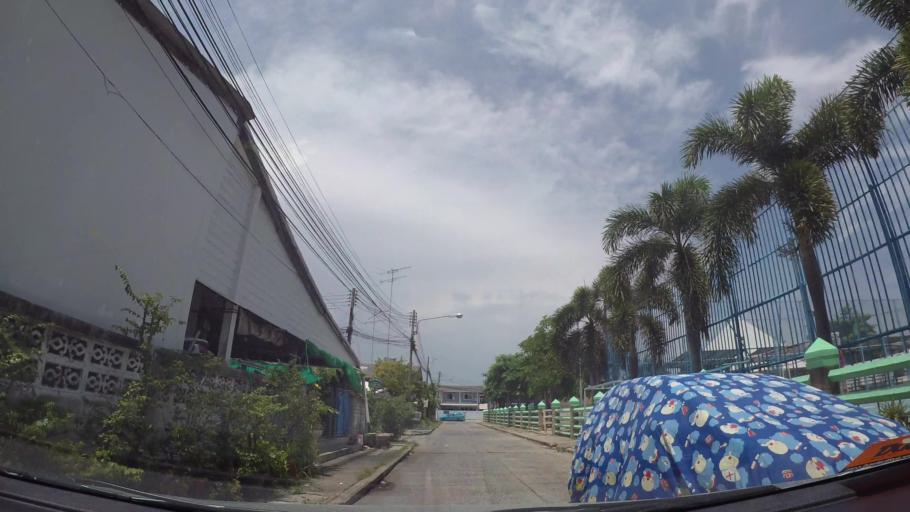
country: TH
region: Chon Buri
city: Chon Buri
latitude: 13.3288
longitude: 100.9421
